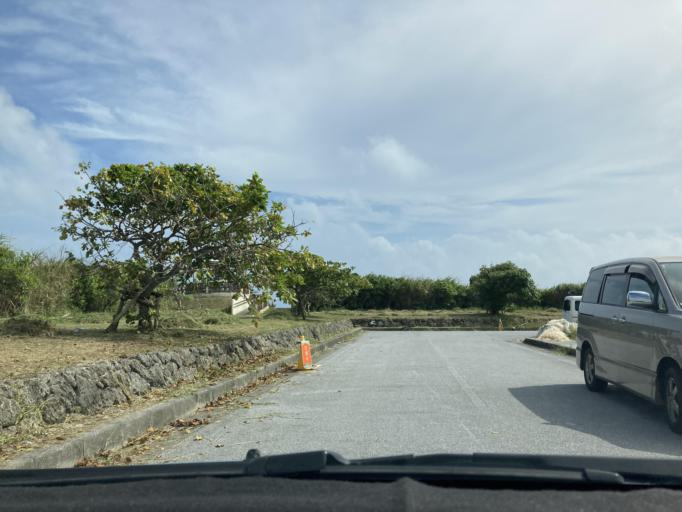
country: JP
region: Okinawa
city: Ginowan
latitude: 26.1491
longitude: 127.8098
